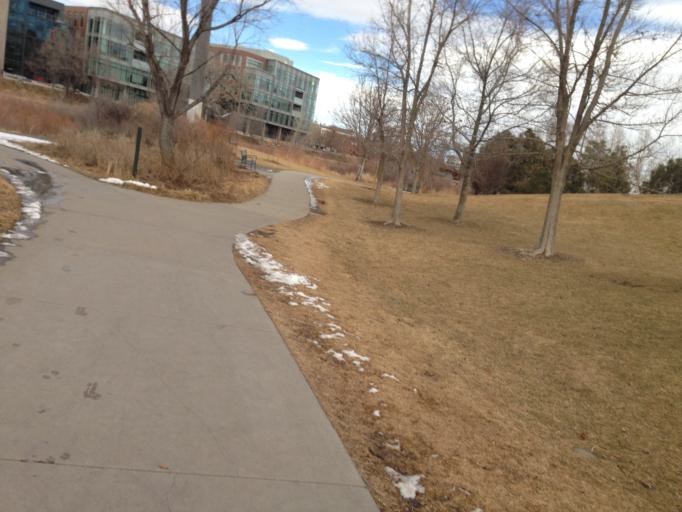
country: US
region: Colorado
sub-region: Denver County
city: Denver
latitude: 39.7562
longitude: -105.0059
